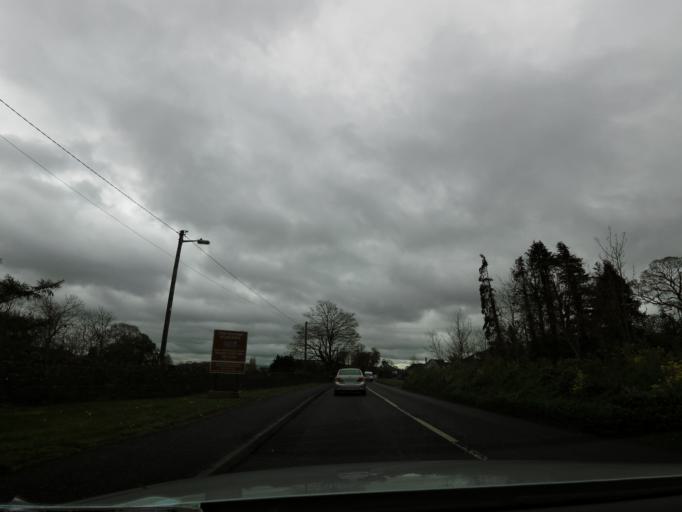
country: IE
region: Leinster
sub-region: Kilkenny
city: Kilkenny
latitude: 52.6711
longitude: -7.2673
